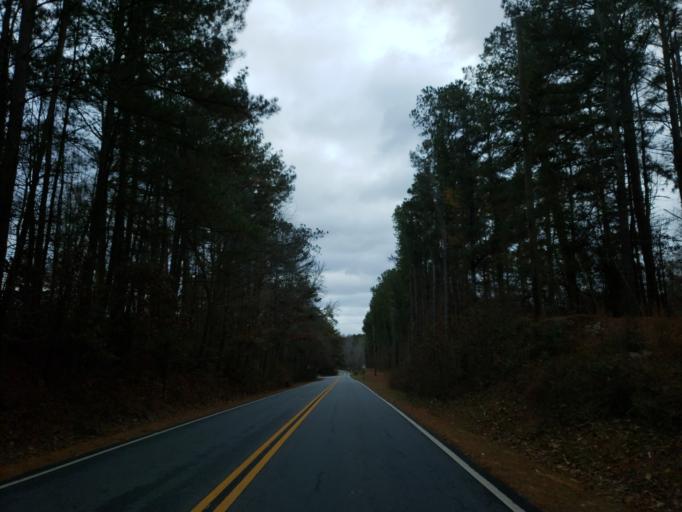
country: US
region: Georgia
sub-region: Cobb County
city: Fair Oaks
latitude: 33.9245
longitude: -84.6014
